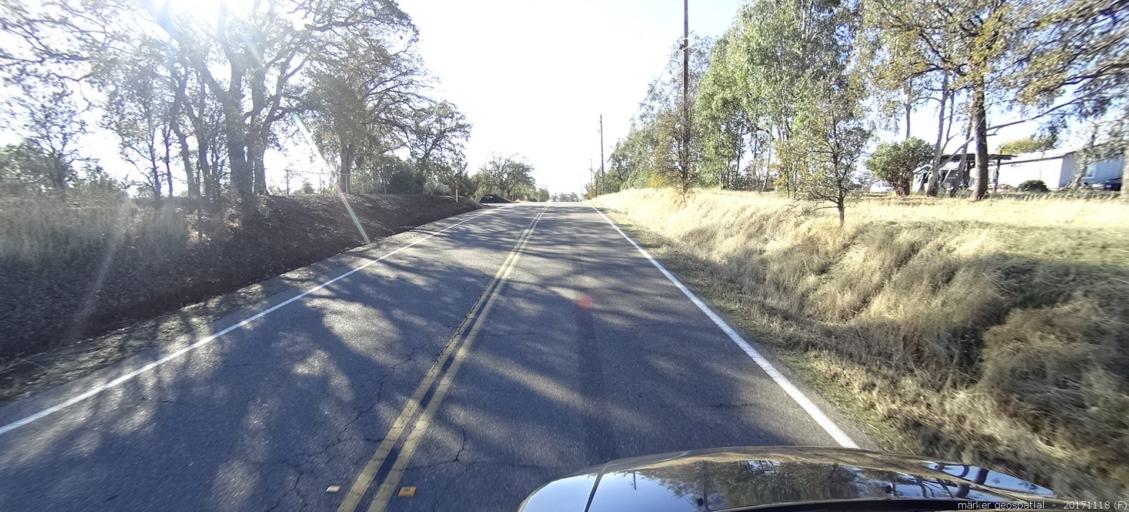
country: US
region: California
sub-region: Shasta County
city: Cottonwood
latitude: 40.4161
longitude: -122.2725
